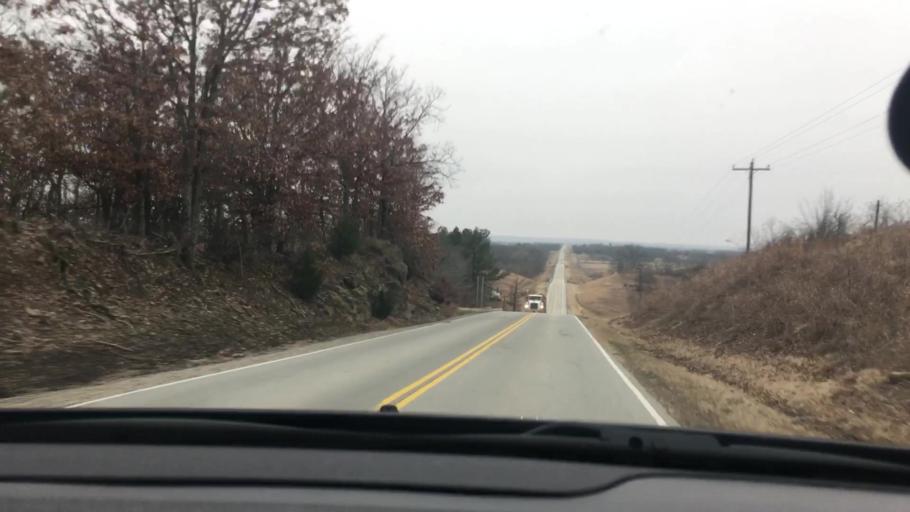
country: US
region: Oklahoma
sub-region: Coal County
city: Coalgate
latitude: 34.5055
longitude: -96.3477
